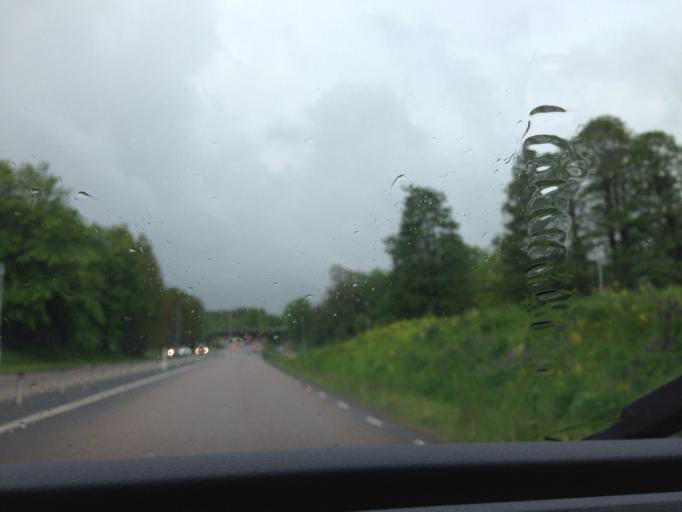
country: SE
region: Vaestra Goetaland
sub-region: Skovde Kommun
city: Skoevde
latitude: 58.3945
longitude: 13.8376
